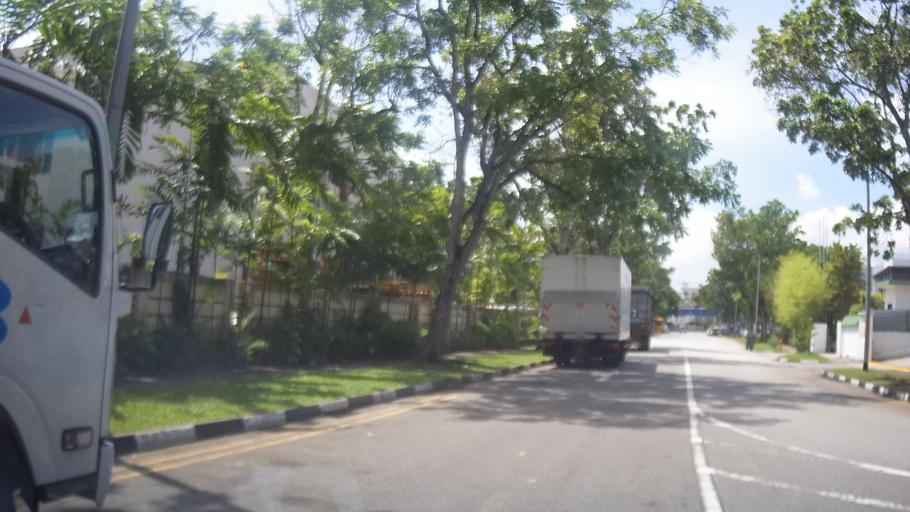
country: MY
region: Johor
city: Johor Bahru
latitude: 1.4069
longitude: 103.7474
